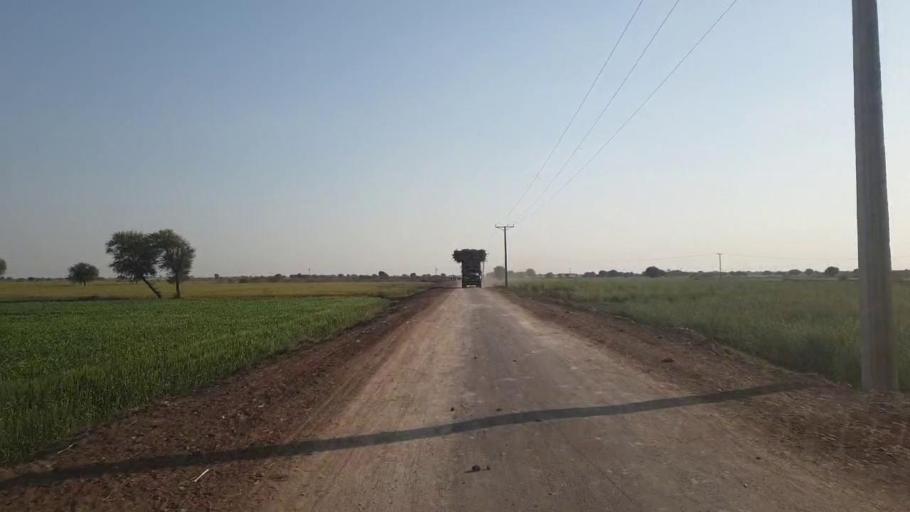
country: PK
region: Sindh
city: Chambar
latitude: 25.2864
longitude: 68.7497
